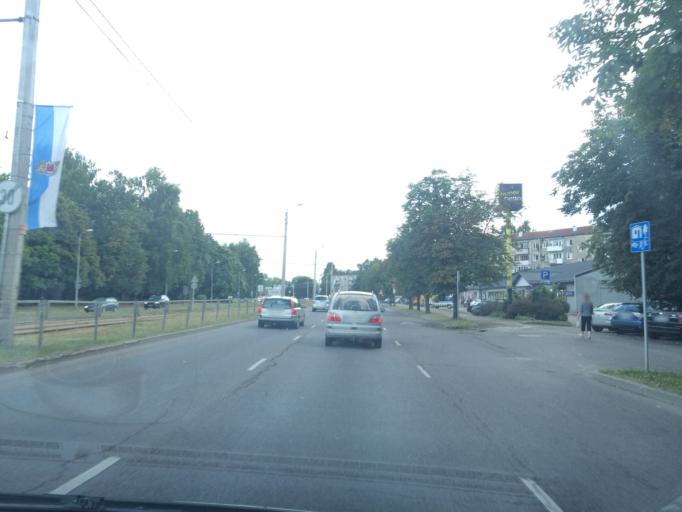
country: LV
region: Kekava
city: Balozi
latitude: 56.9118
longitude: 24.1777
